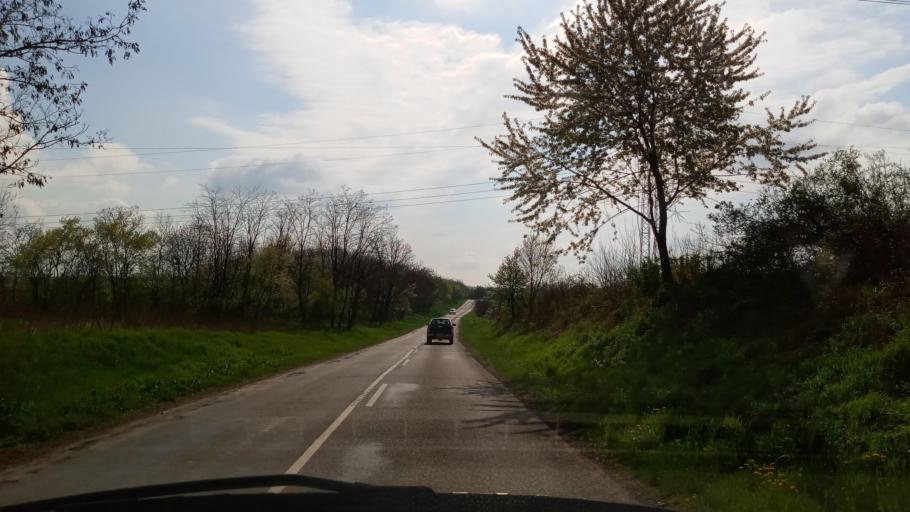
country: HU
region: Baranya
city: Pecsvarad
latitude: 46.1531
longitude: 18.4418
